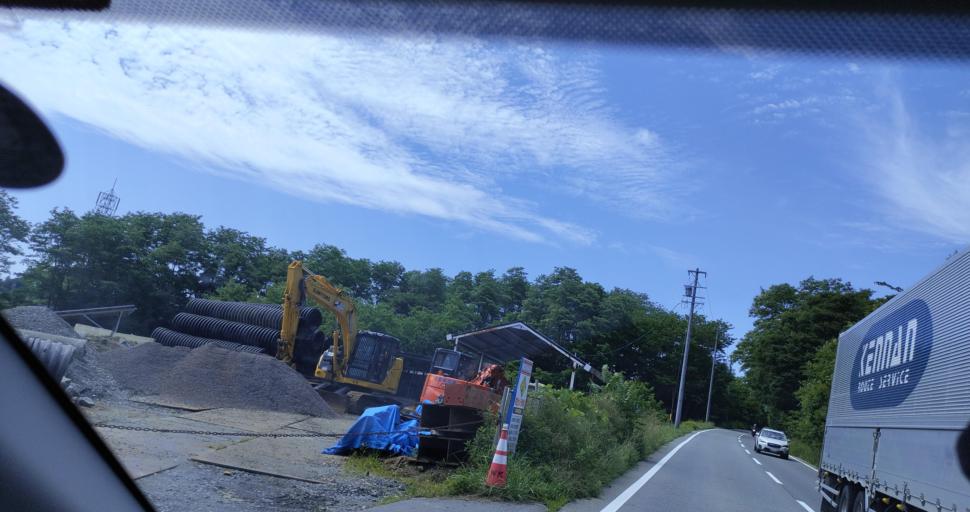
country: JP
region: Nagano
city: Ueda
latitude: 36.3839
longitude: 138.3287
